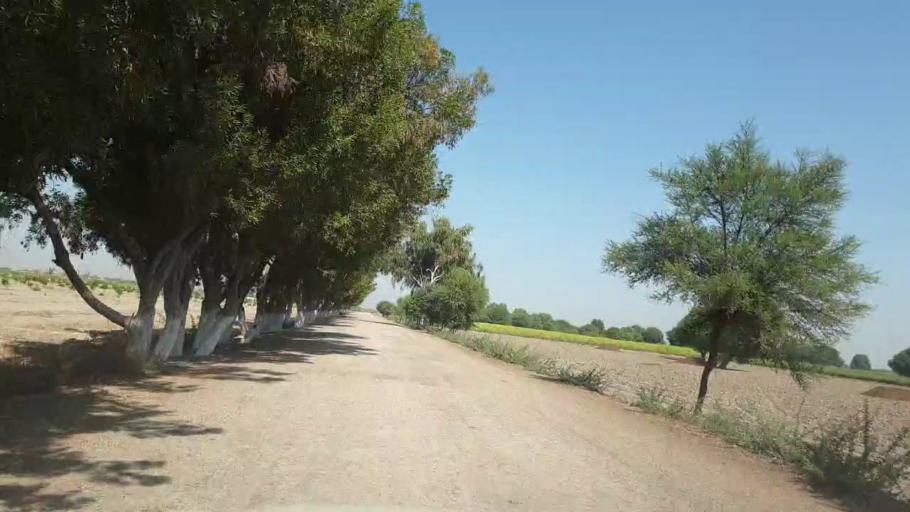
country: PK
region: Sindh
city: Kunri
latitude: 25.1333
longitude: 69.5094
